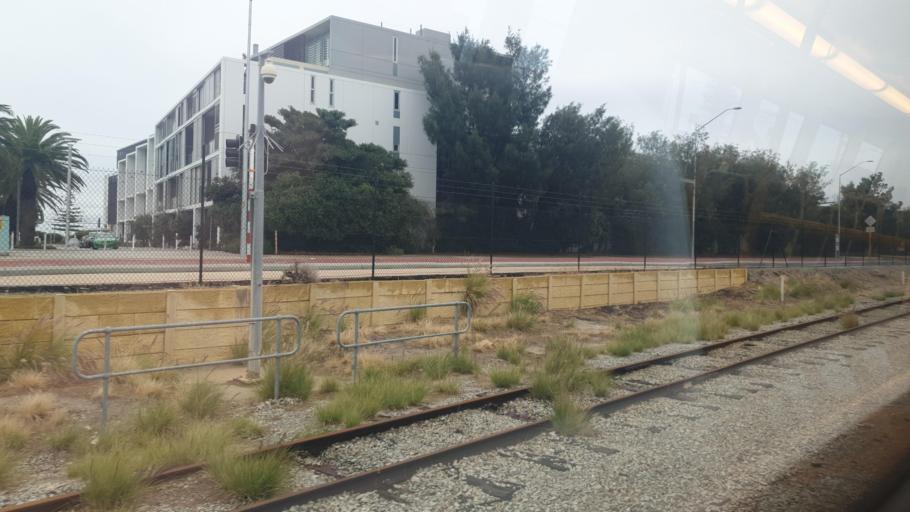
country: AU
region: Western Australia
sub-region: Fremantle
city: North Fremantle
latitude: -32.0294
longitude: 115.7518
